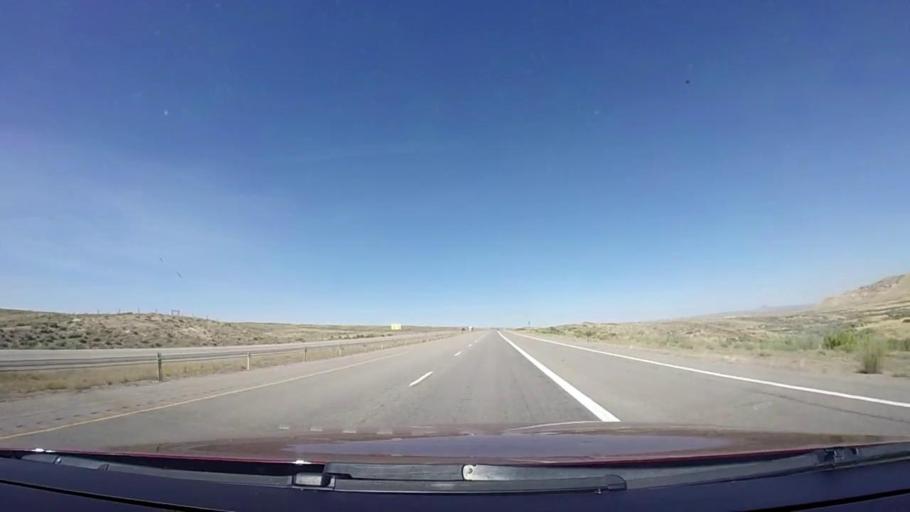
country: US
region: Wyoming
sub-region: Sweetwater County
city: Rock Springs
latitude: 41.6477
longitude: -108.6865
